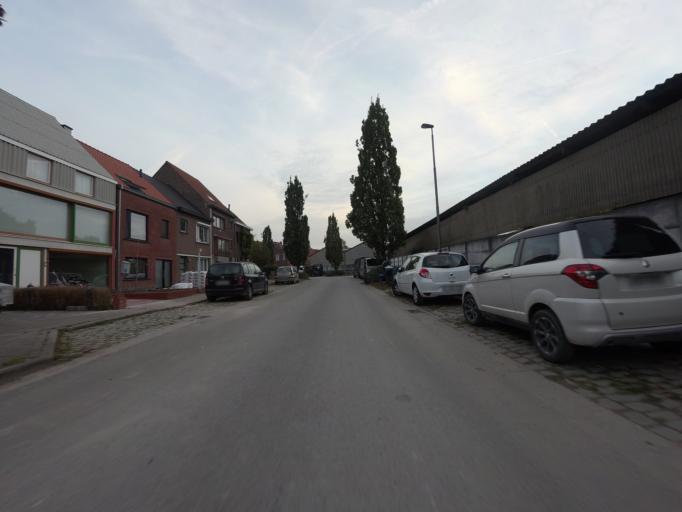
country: BE
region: Flanders
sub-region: Provincie Oost-Vlaanderen
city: Ledeberg
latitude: 51.0677
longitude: 3.7482
